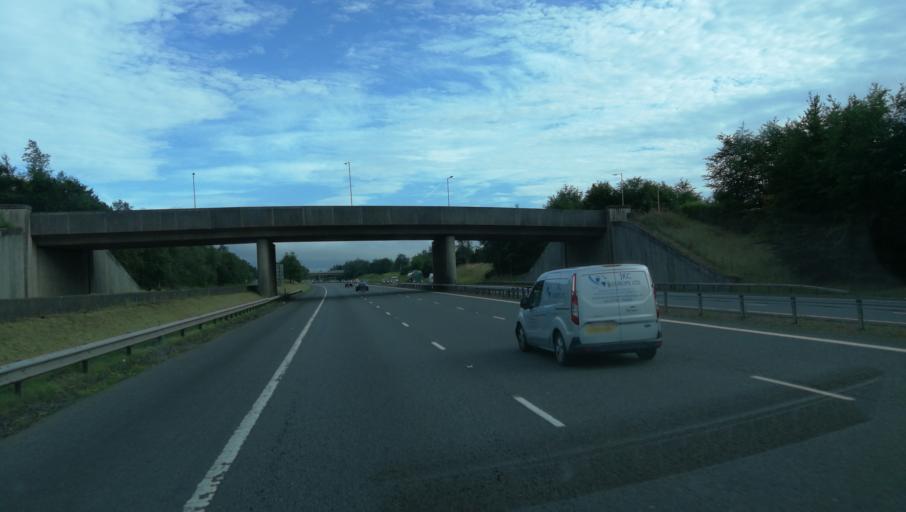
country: GB
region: Scotland
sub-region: Dumfries and Galloway
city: Lockerbie
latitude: 55.1196
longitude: -3.3620
